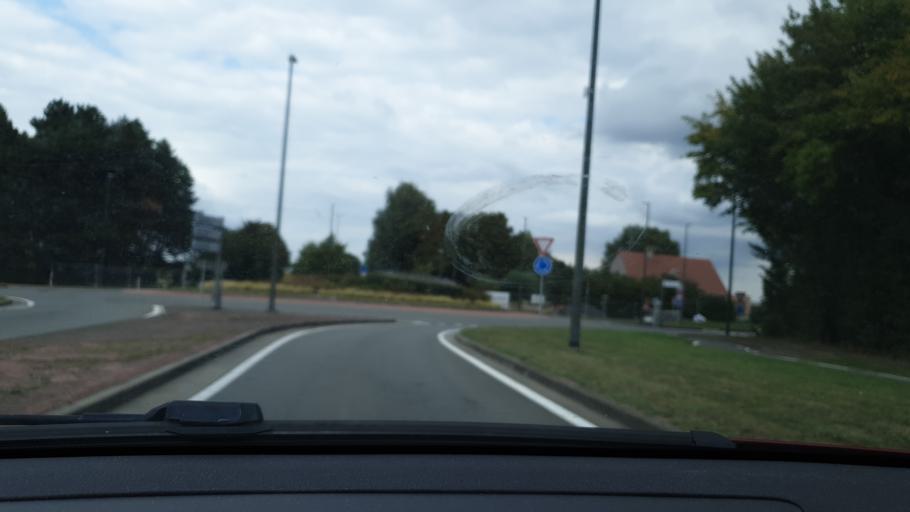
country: BE
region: Wallonia
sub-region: Province du Hainaut
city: Ath
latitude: 50.6359
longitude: 3.7626
